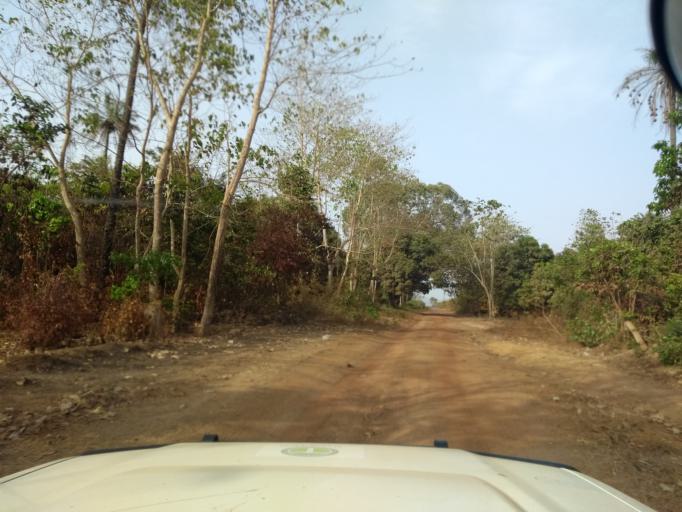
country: GN
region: Kindia
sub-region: Prefecture de Dubreka
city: Dubreka
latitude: 9.8510
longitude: -13.5547
